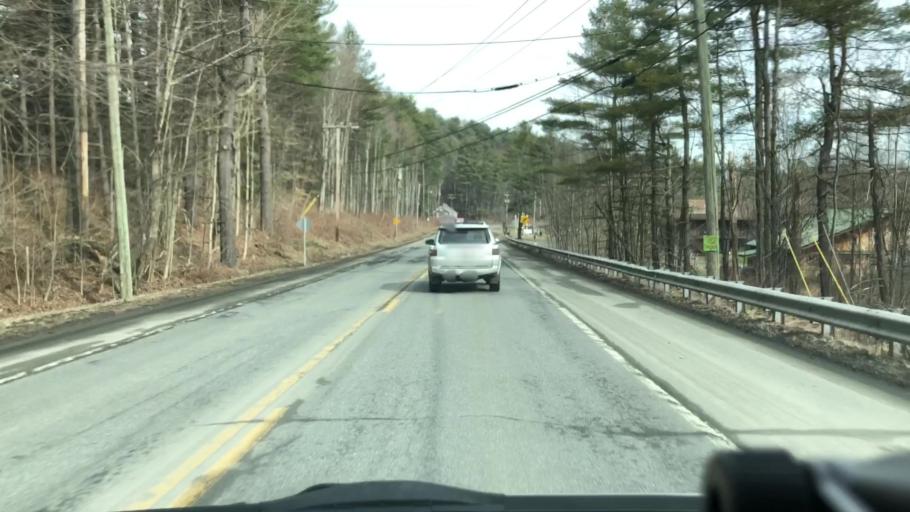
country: US
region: Massachusetts
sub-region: Franklin County
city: Shelburne
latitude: 42.6016
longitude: -72.6711
